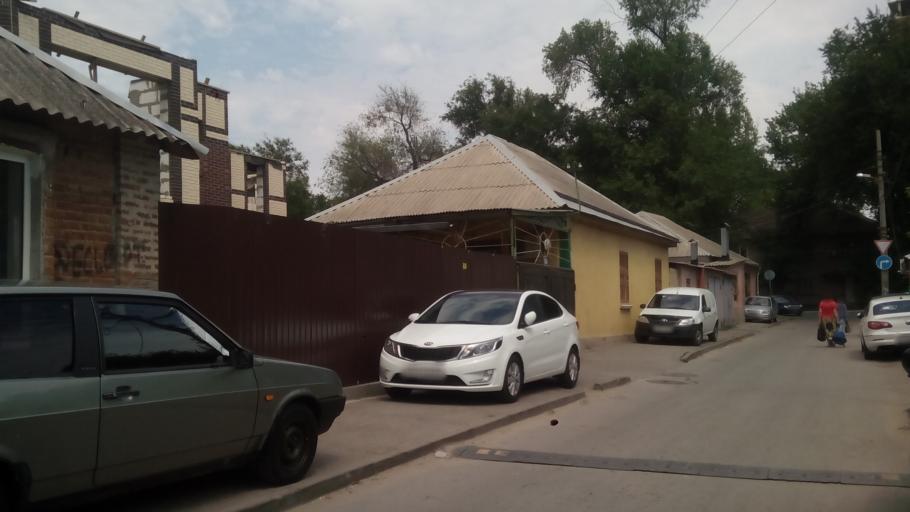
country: RU
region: Rostov
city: Rostov-na-Donu
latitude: 47.2481
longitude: 39.7416
